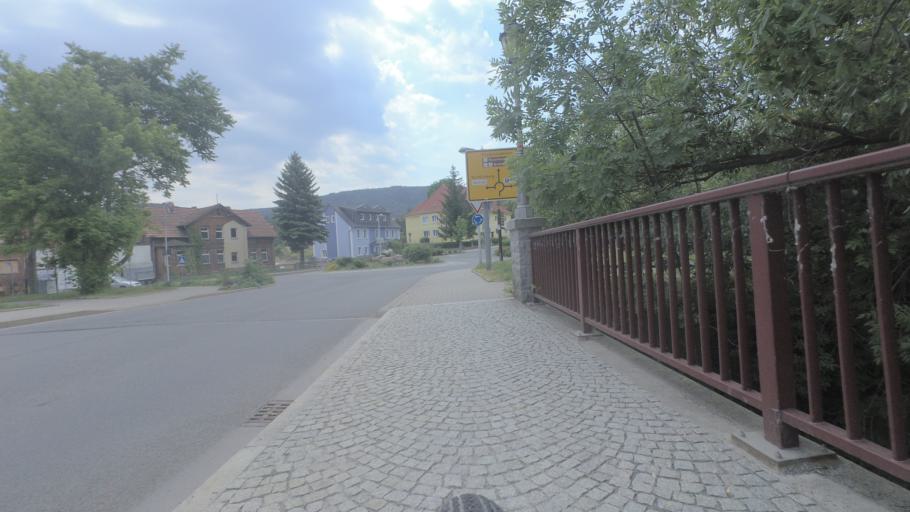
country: DE
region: Saxony-Anhalt
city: Thale
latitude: 51.7509
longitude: 11.0335
